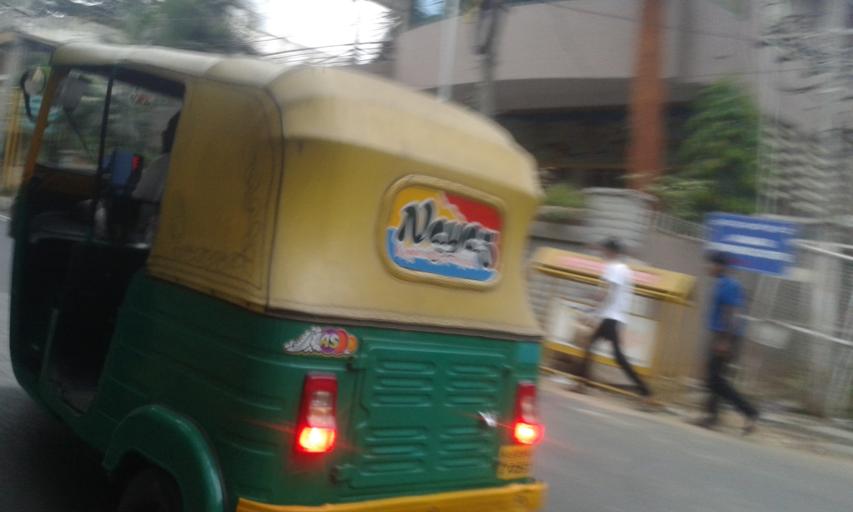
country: IN
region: Karnataka
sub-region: Bangalore Urban
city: Bangalore
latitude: 12.9286
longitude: 77.5895
